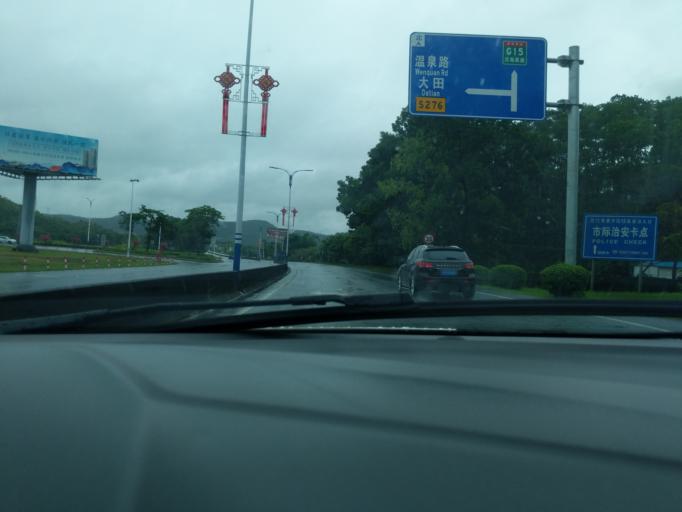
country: CN
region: Guangdong
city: Pingshi
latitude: 22.2330
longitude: 112.3103
